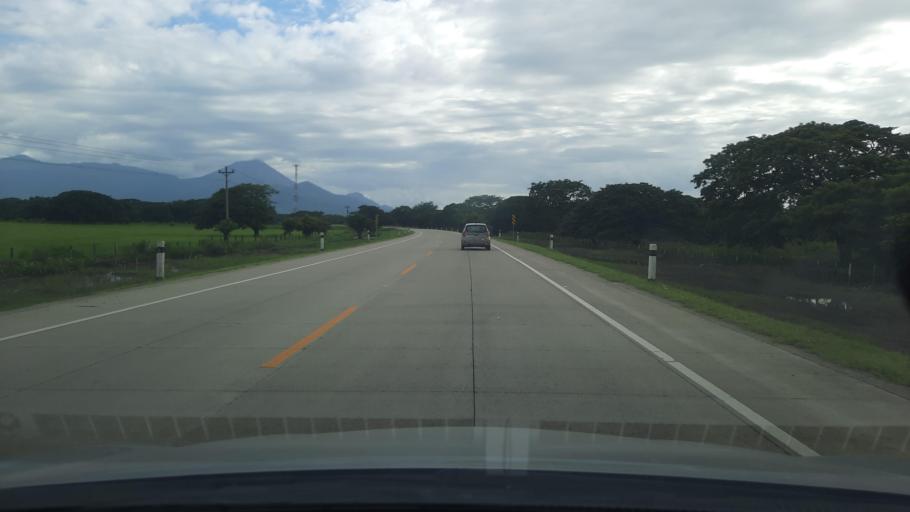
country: NI
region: Chinandega
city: Somotillo
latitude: 12.8369
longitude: -86.8900
